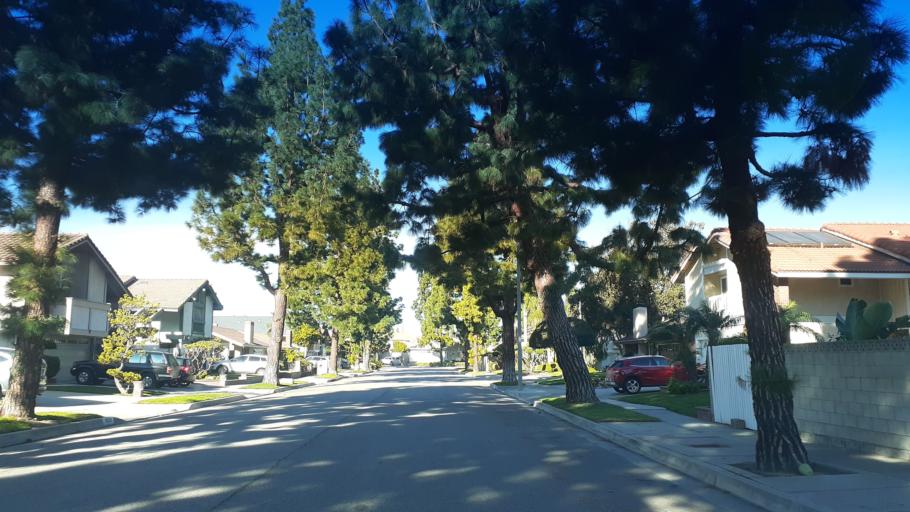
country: US
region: California
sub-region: Los Angeles County
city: Cerritos
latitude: 33.8519
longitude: -118.0669
